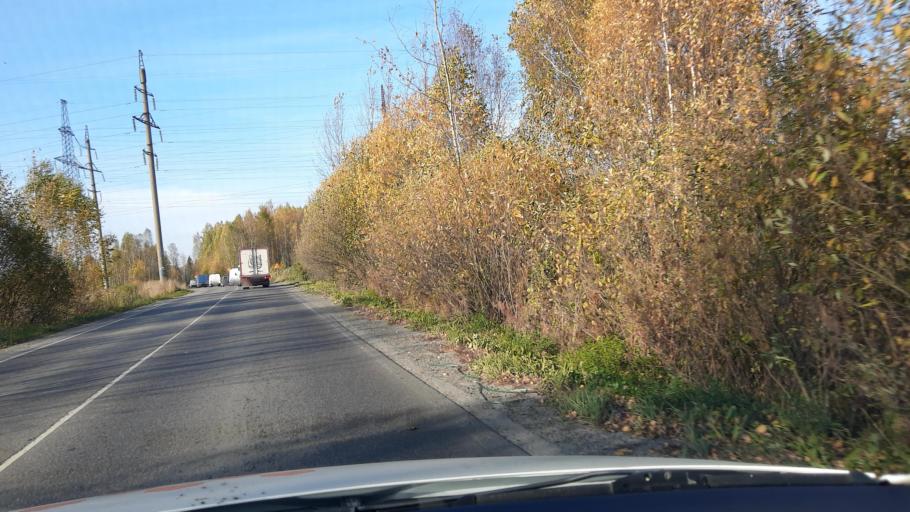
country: RU
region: Moskovskaya
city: Fryazevo
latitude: 55.7541
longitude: 38.5211
